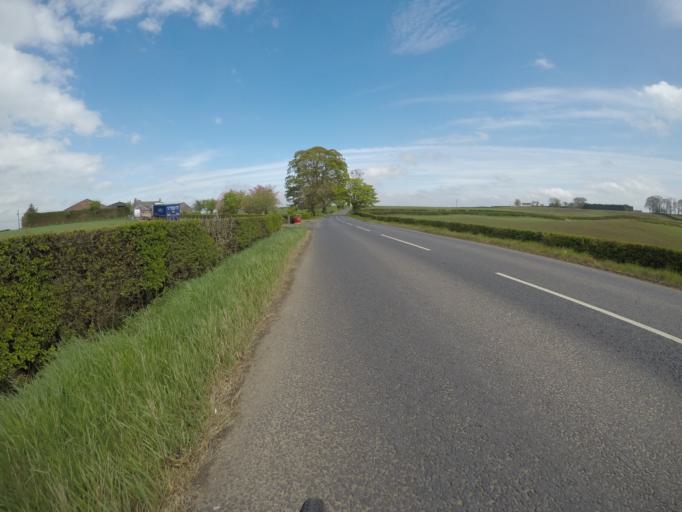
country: GB
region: Scotland
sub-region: East Ayrshire
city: Crosshouse
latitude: 55.6511
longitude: -4.5677
